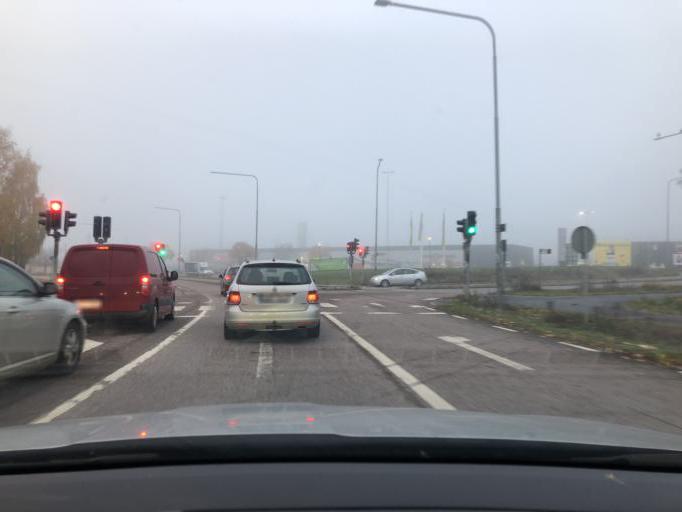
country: SE
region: Stockholm
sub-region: Botkyrka Kommun
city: Fittja
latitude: 59.2516
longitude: 17.8763
